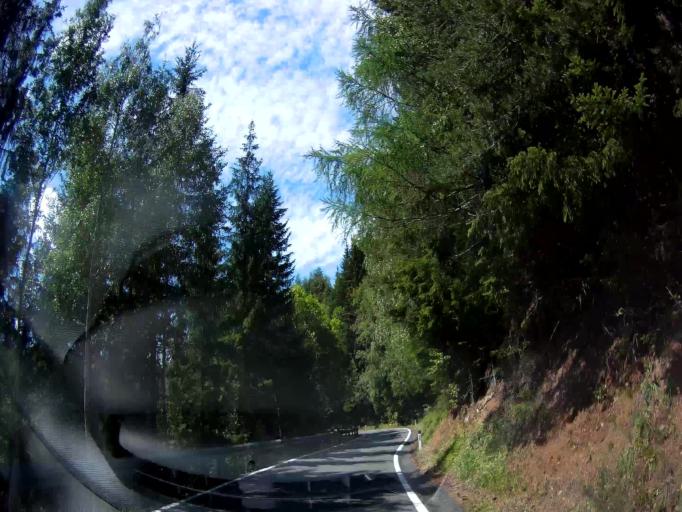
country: AT
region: Carinthia
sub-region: Politischer Bezirk Sankt Veit an der Glan
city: Glodnitz
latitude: 46.9203
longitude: 14.0584
